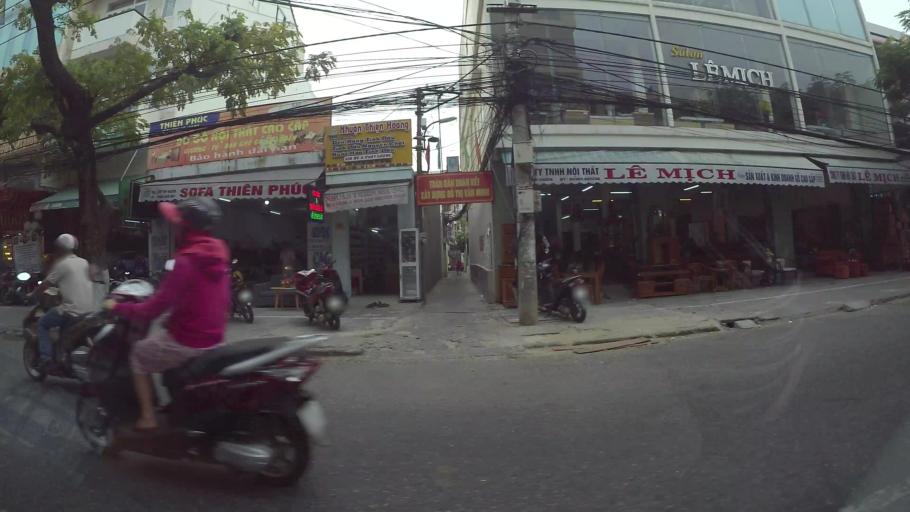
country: VN
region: Da Nang
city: Da Nang
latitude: 16.0638
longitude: 108.2154
